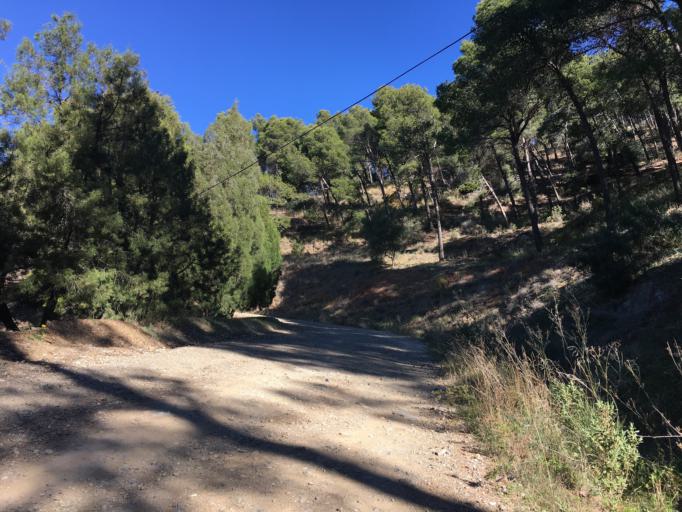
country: ES
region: Andalusia
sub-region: Provincia de Malaga
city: Malaga
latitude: 36.7806
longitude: -4.3858
